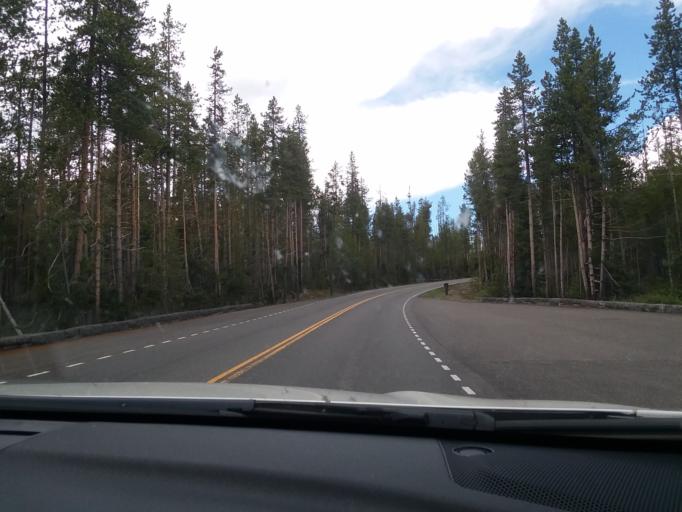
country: US
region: Idaho
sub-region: Teton County
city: Driggs
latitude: 44.1520
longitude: -110.6737
